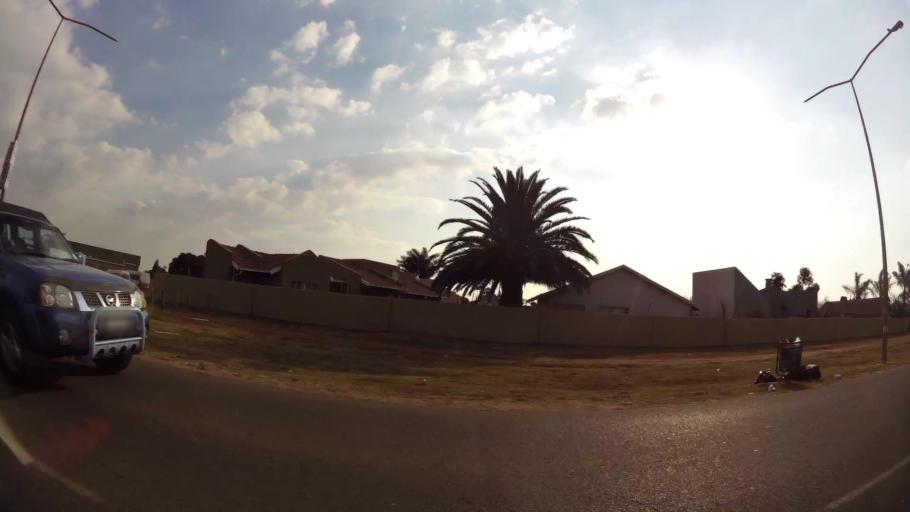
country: ZA
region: Gauteng
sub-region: City of Johannesburg Metropolitan Municipality
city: Modderfontein
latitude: -26.0982
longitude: 28.1974
